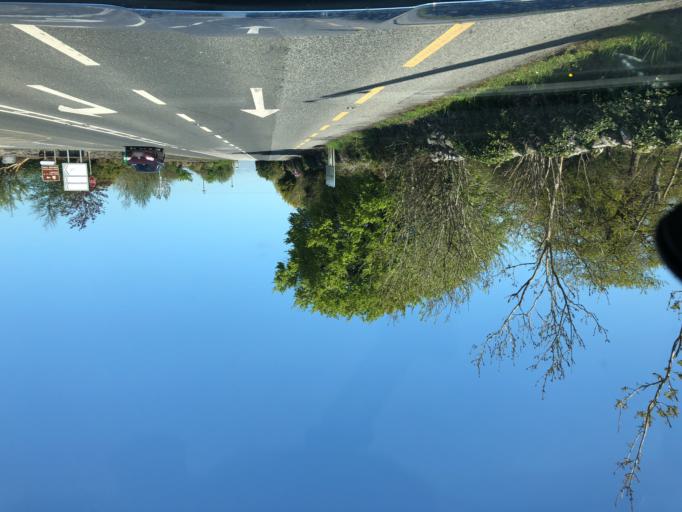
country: IE
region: Connaught
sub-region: County Galway
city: Athenry
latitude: 53.2358
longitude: -8.7453
